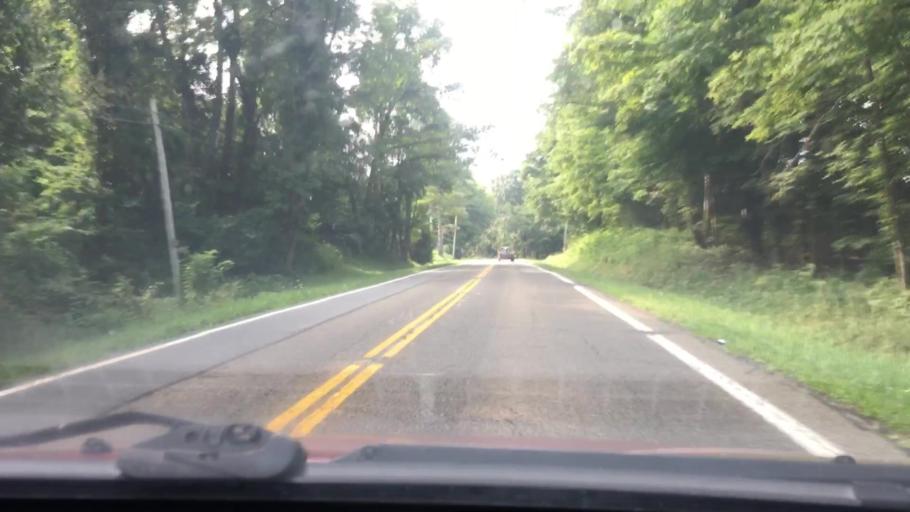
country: US
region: Ohio
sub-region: Belmont County
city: Barnesville
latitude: 40.1193
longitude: -81.2180
